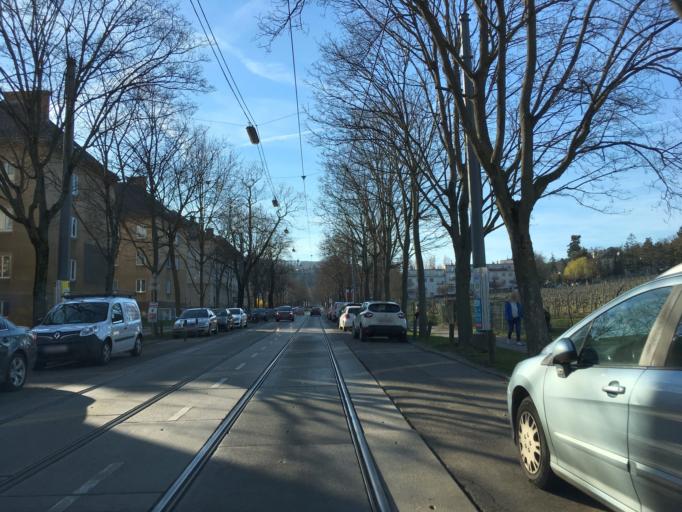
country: AT
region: Vienna
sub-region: Wien Stadt
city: Vienna
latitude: 48.2296
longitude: 16.3014
